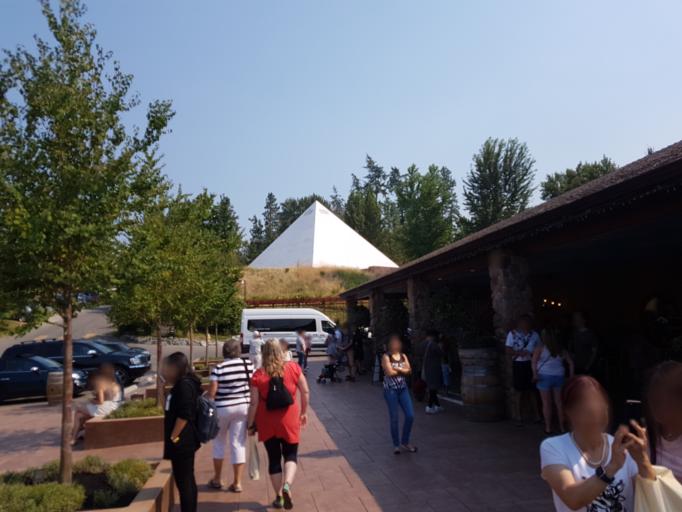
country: CA
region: British Columbia
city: Kelowna
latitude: 49.8065
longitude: -119.5015
